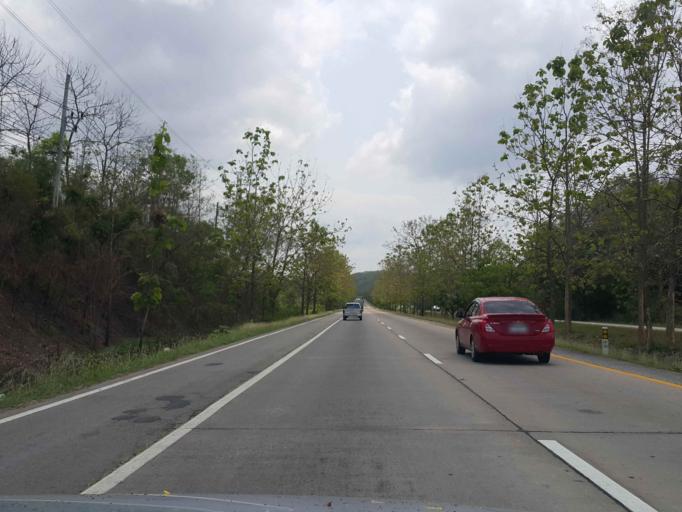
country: TH
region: Lamphun
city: Mae Tha
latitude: 18.5167
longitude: 99.0917
